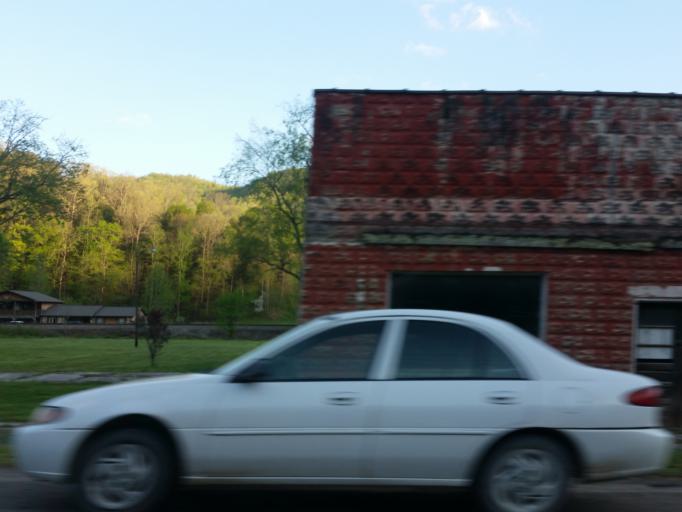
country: US
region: Tennessee
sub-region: Campbell County
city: Fincastle
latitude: 36.5661
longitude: -83.9341
